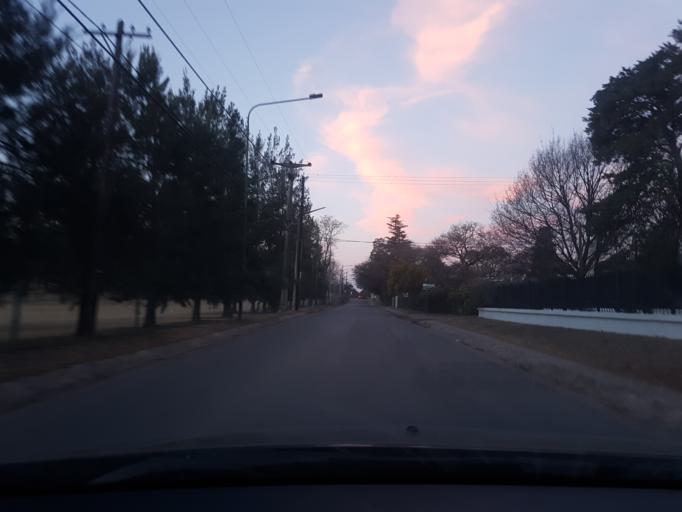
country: AR
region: Cordoba
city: Villa Allende
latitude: -31.2842
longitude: -64.2914
